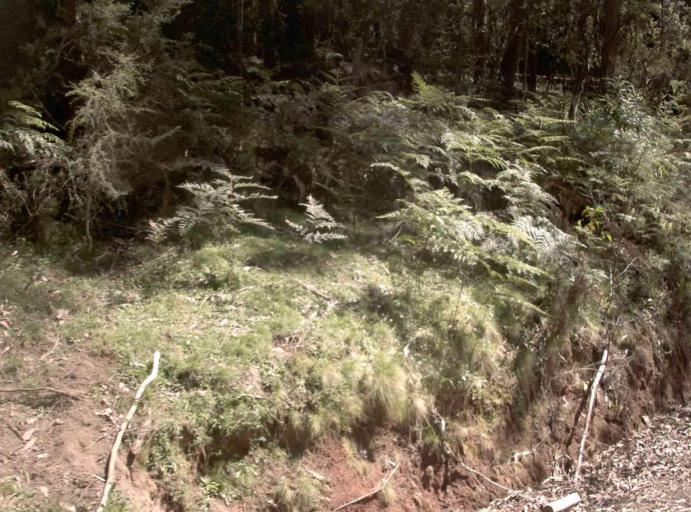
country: AU
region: New South Wales
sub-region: Bombala
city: Bombala
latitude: -37.0693
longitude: 148.7879
